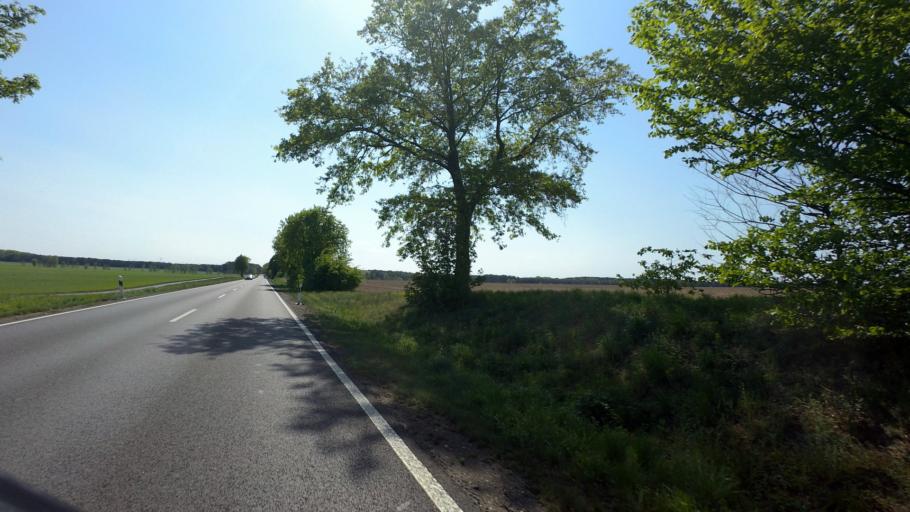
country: DE
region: Brandenburg
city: Tauche
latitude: 52.0767
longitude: 14.1582
